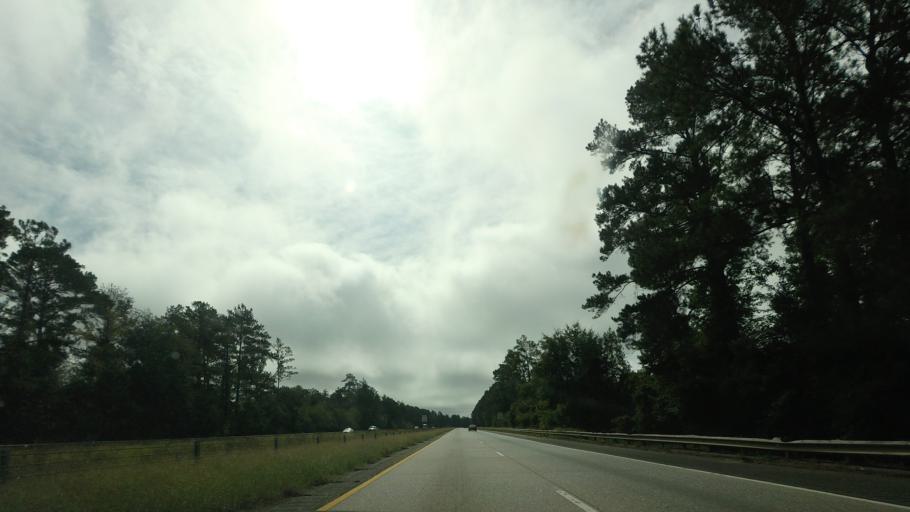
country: US
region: Georgia
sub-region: Bibb County
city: Macon
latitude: 32.7902
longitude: -83.5628
